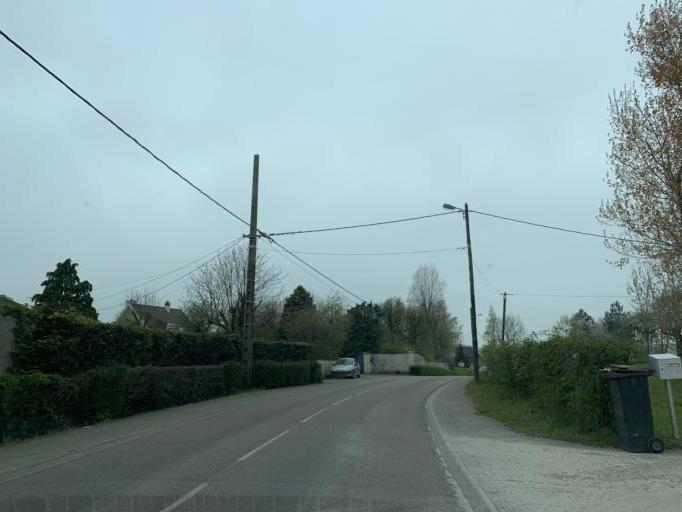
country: FR
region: Nord-Pas-de-Calais
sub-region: Departement du Pas-de-Calais
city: Rinxent
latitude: 50.7804
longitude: 1.7343
